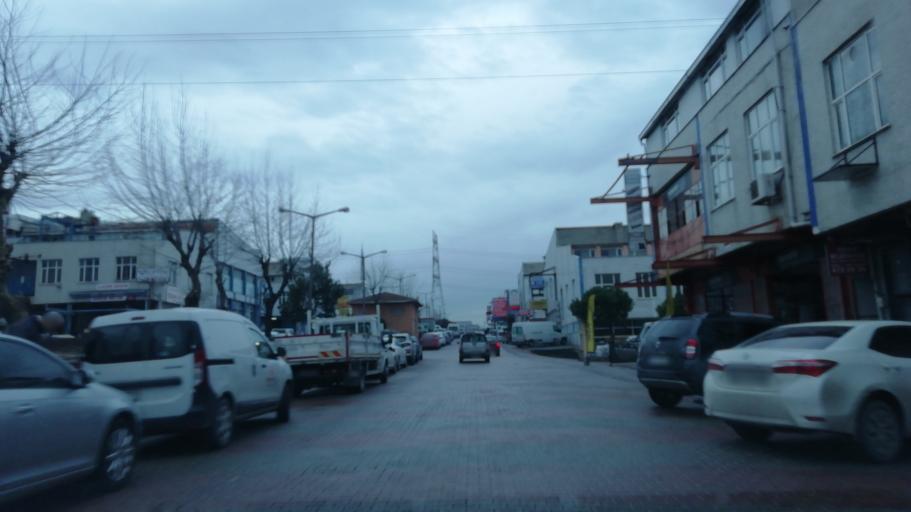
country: TR
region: Istanbul
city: Mahmutbey
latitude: 41.0661
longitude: 28.8064
